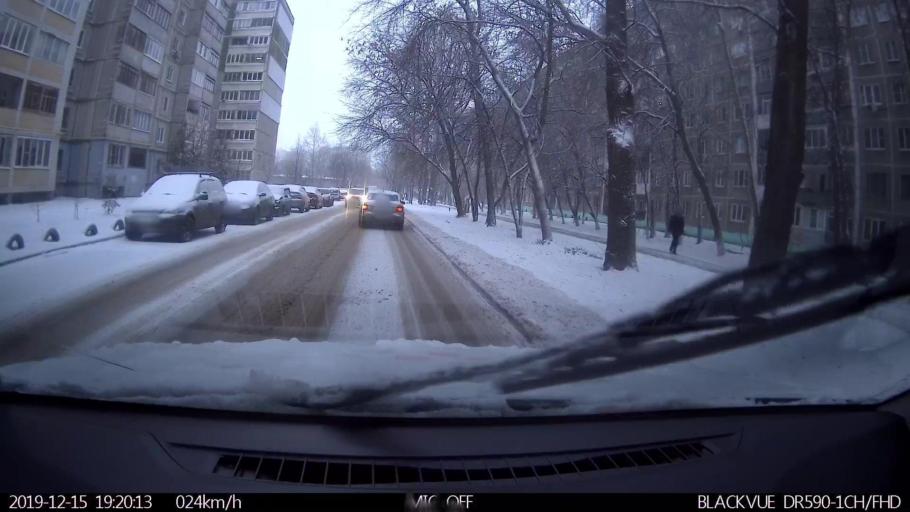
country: RU
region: Nizjnij Novgorod
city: Neklyudovo
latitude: 56.3545
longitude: 43.8581
